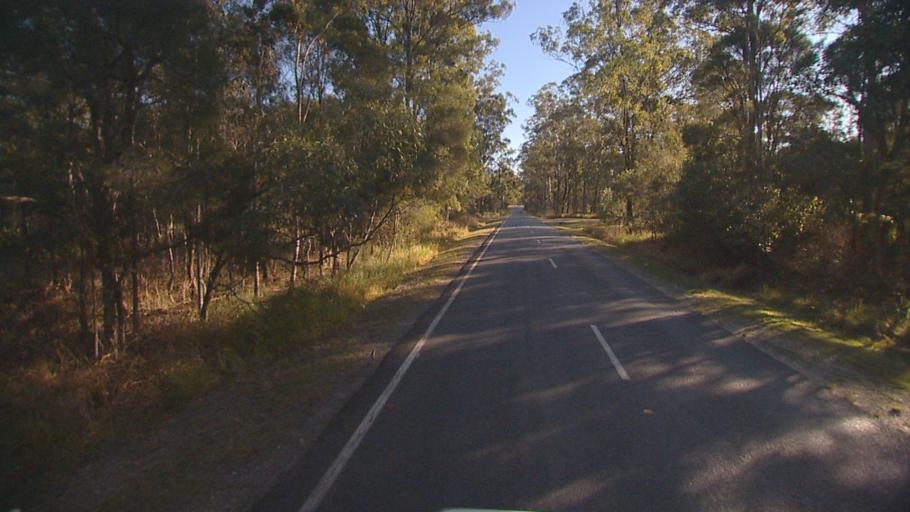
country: AU
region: Queensland
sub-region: Logan
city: Chambers Flat
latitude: -27.7797
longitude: 153.0698
